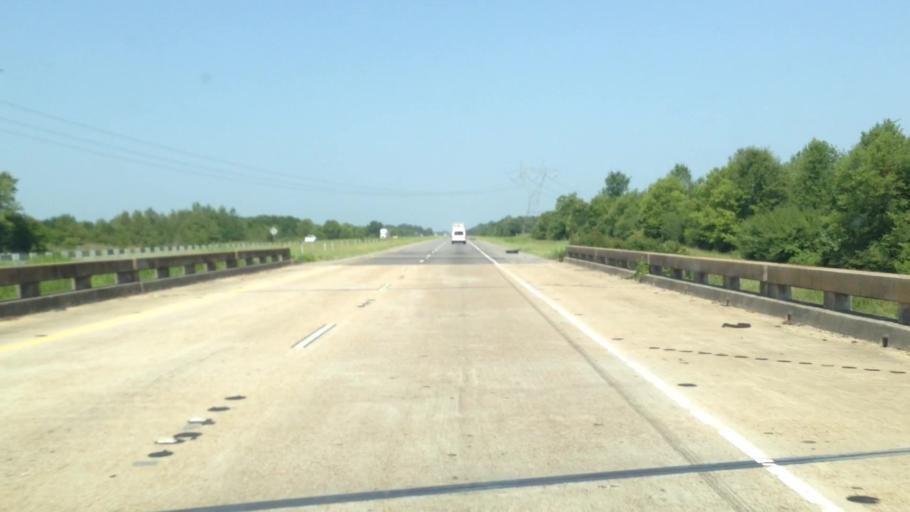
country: US
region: Louisiana
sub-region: Madison Parish
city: Tallulah
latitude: 32.4197
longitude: -91.3025
